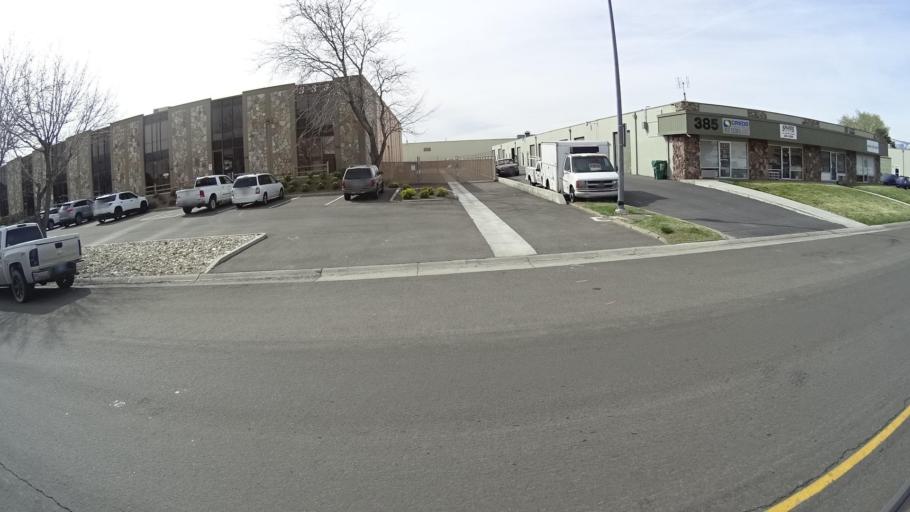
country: US
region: Nevada
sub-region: Washoe County
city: Sparks
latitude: 39.5250
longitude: -119.7466
